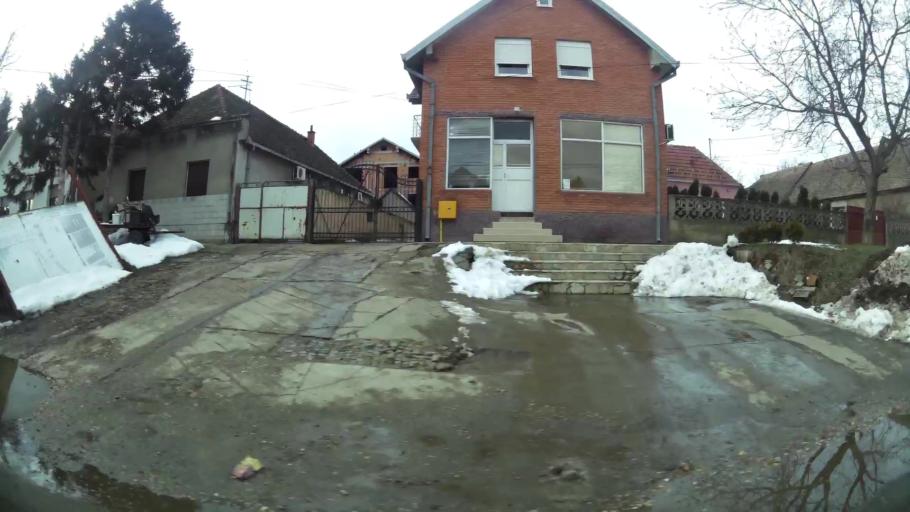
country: RS
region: Central Serbia
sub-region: Belgrade
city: Surcin
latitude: 44.7976
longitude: 20.2844
